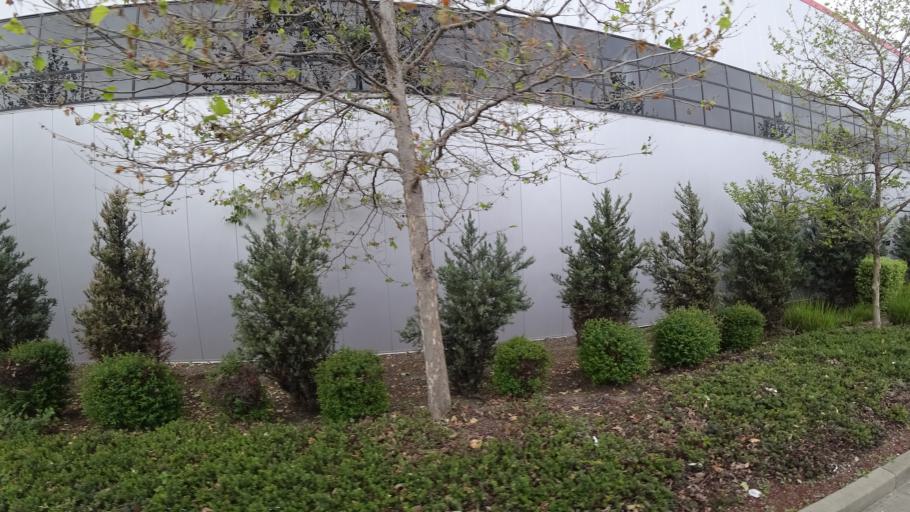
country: US
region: California
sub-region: Alameda County
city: San Lorenzo
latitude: 37.6632
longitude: -122.1198
